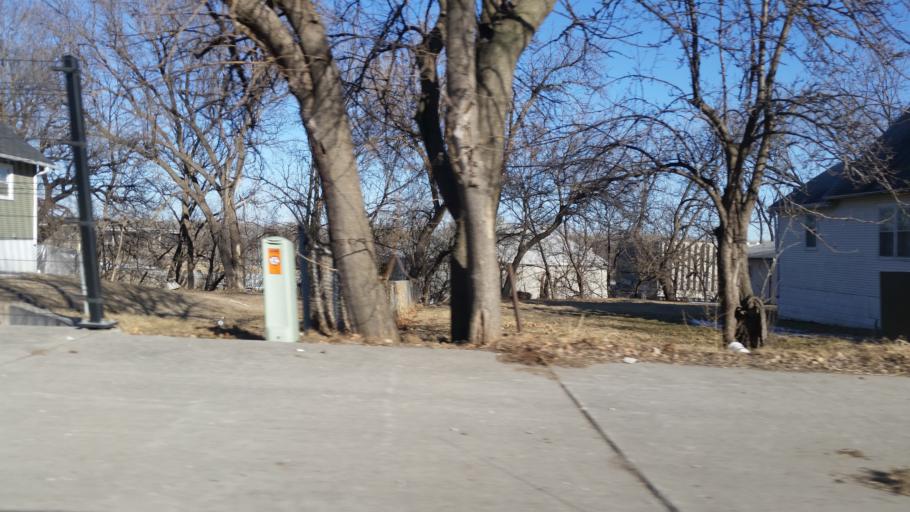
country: US
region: Nebraska
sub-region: Douglas County
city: Omaha
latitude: 41.2084
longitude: -95.9334
